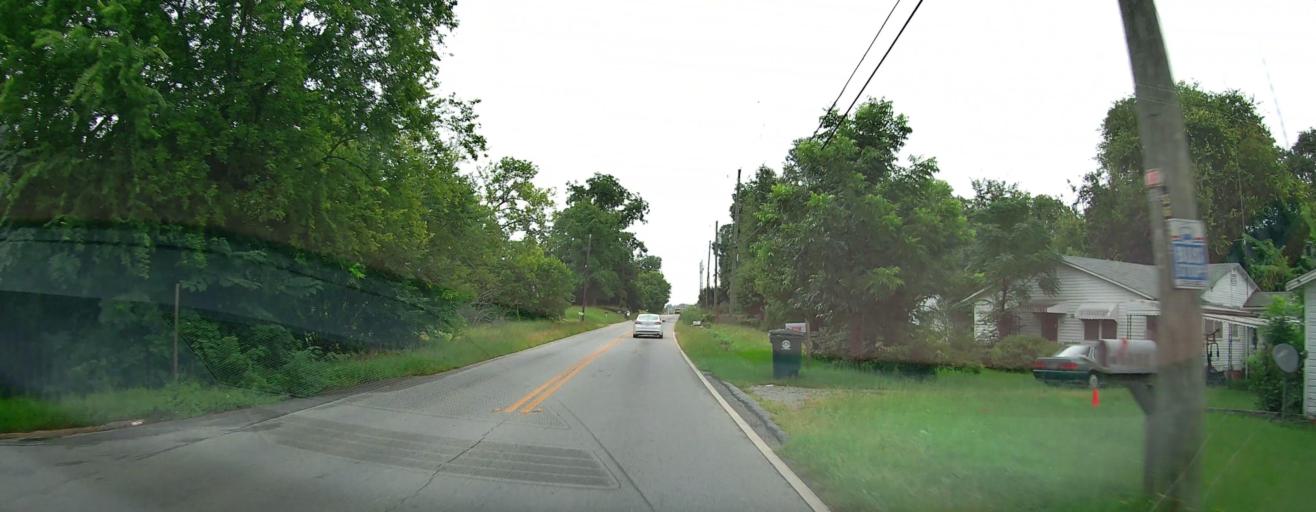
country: US
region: Georgia
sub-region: Bibb County
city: Macon
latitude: 32.7881
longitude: -83.6578
